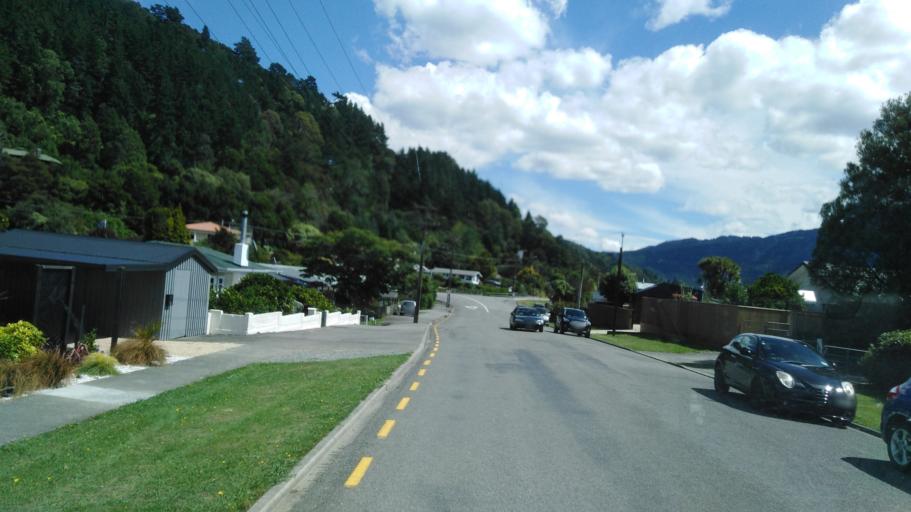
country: NZ
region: Marlborough
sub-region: Marlborough District
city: Picton
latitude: -41.2756
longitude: 173.7664
